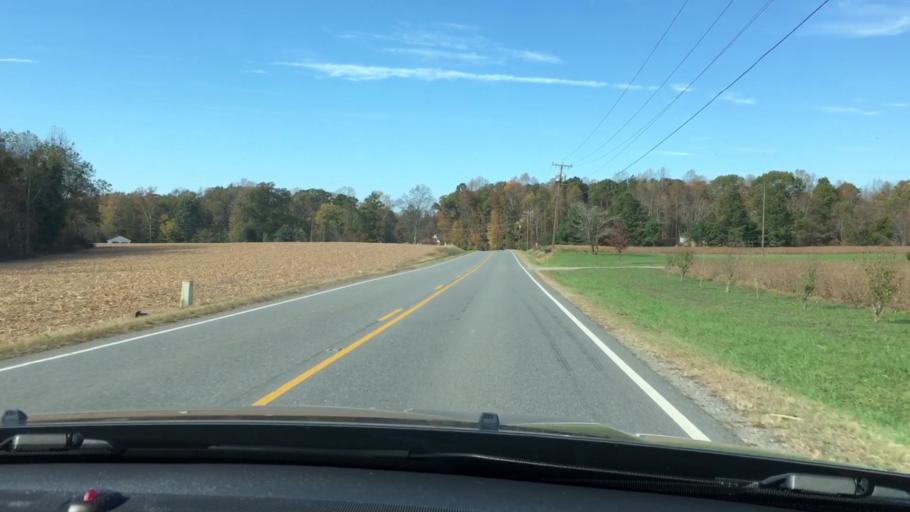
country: US
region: Virginia
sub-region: King William County
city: West Point
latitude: 37.5887
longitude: -76.8563
